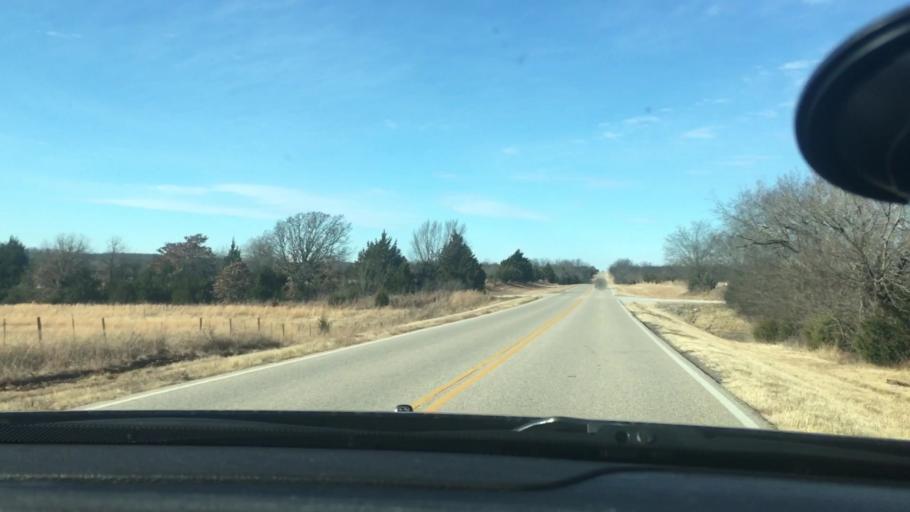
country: US
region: Oklahoma
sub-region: Garvin County
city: Stratford
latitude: 34.9859
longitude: -97.0005
